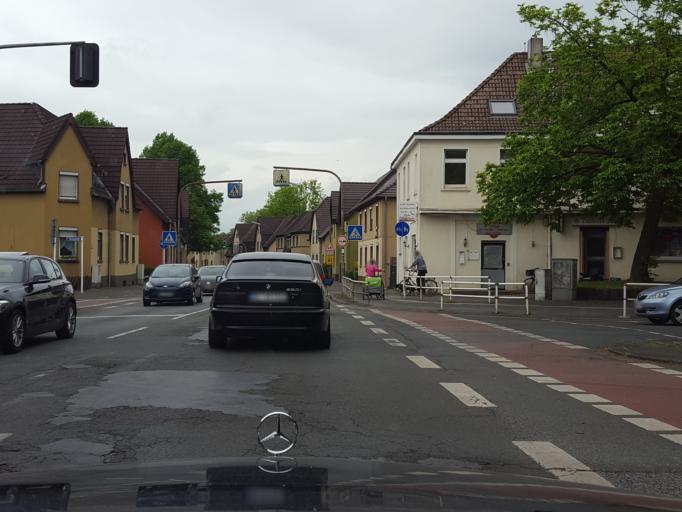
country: DE
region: North Rhine-Westphalia
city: Marl
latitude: 51.6700
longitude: 7.1283
